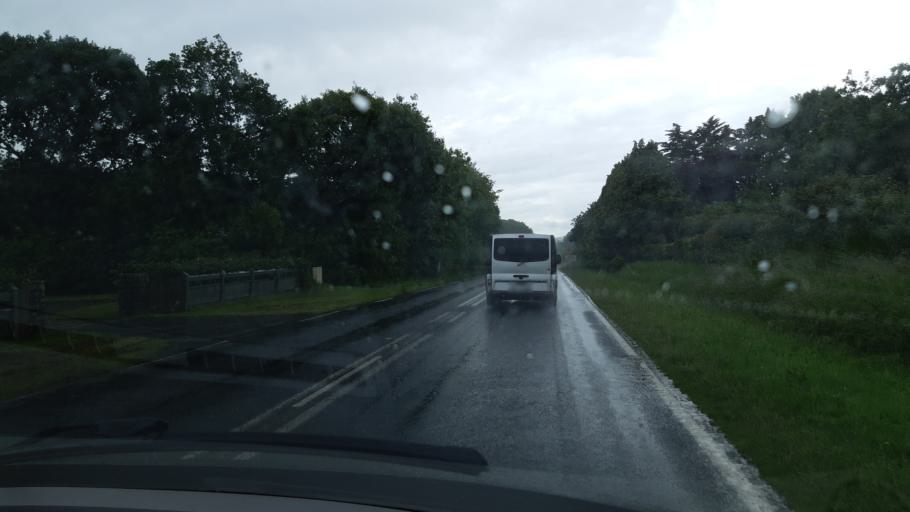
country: FR
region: Brittany
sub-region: Departement du Finistere
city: Plouvorn
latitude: 48.5735
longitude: -4.0481
